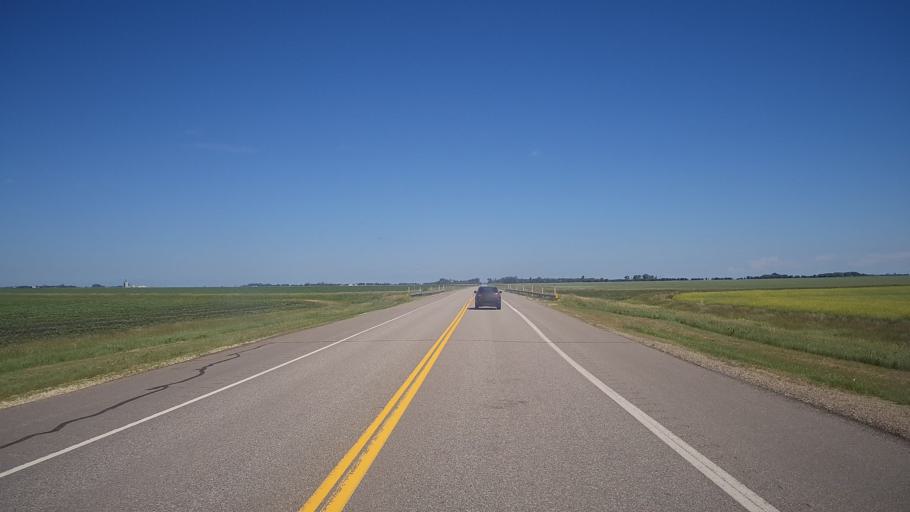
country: CA
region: Manitoba
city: Portage la Prairie
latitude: 50.0326
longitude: -98.4684
